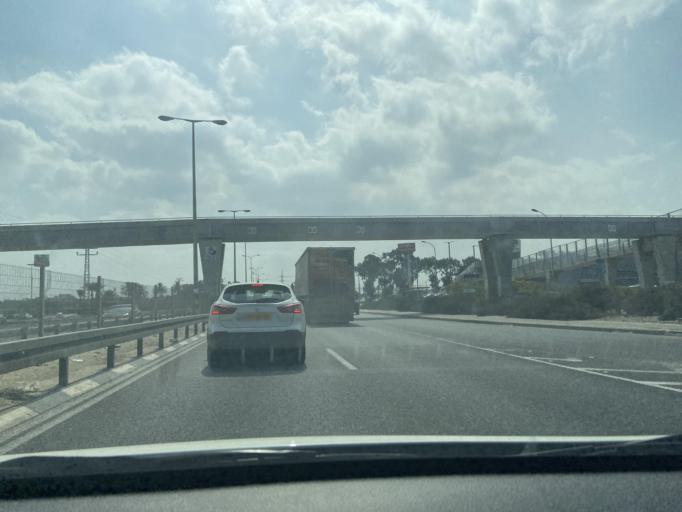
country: IL
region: Northern District
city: `Akko
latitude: 32.9005
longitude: 35.0915
